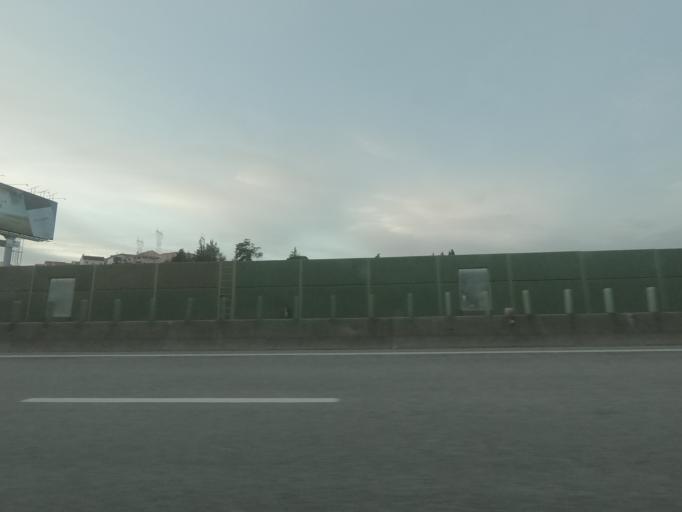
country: PT
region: Lisbon
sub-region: Vila Franca de Xira
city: Sobralinho
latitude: 38.9073
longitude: -9.0368
